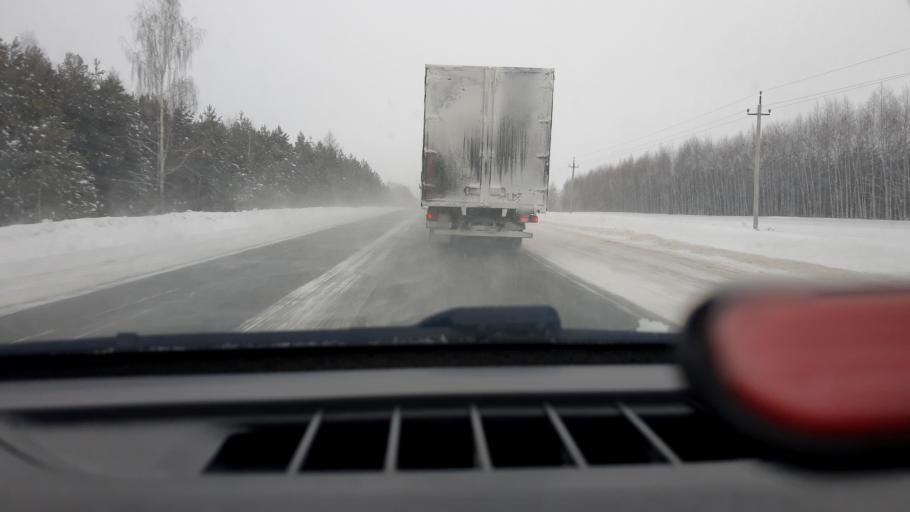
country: RU
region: Nizjnij Novgorod
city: Bol'shoye Murashkino
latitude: 55.9222
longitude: 44.6977
